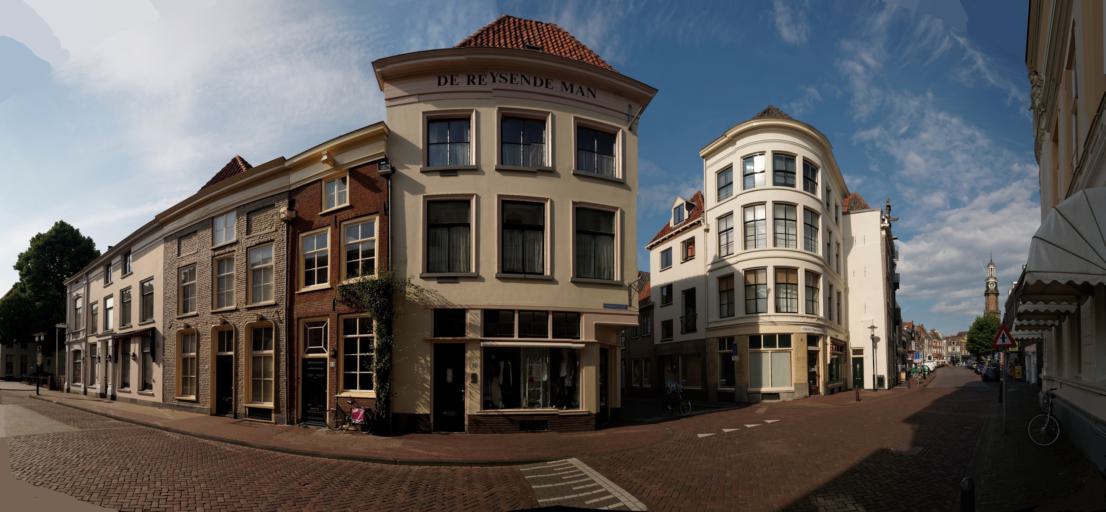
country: NL
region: Gelderland
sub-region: Gemeente Zutphen
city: Zutphen
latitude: 52.1414
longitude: 6.1930
